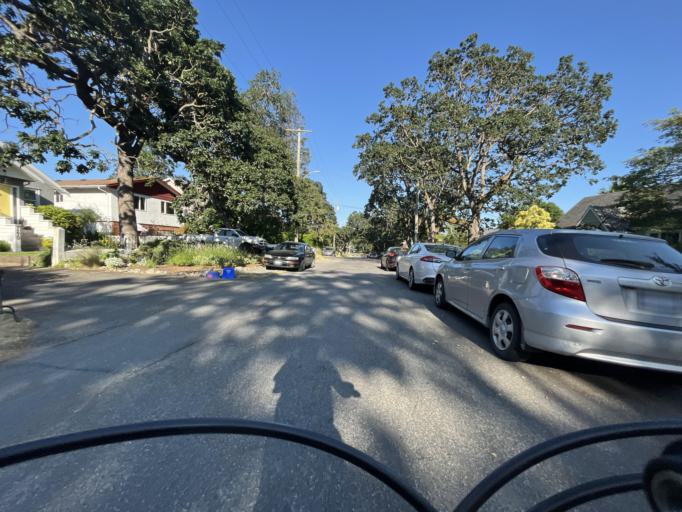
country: CA
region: British Columbia
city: Victoria
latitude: 48.4385
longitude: -123.3477
